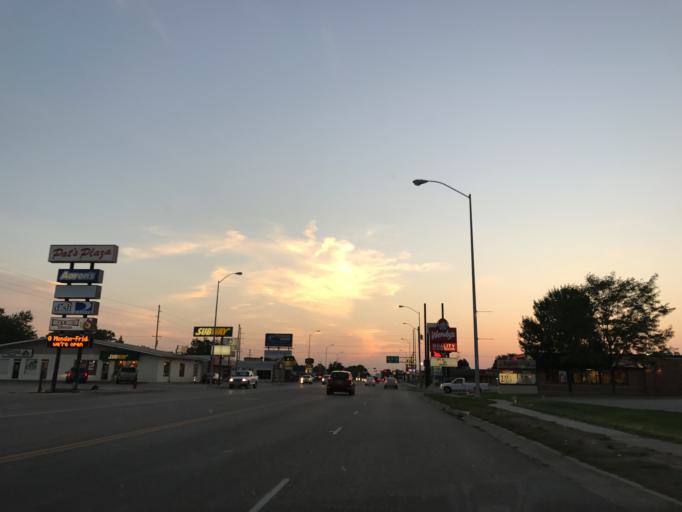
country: US
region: Nebraska
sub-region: Platte County
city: Columbus
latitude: 41.4387
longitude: -97.3640
